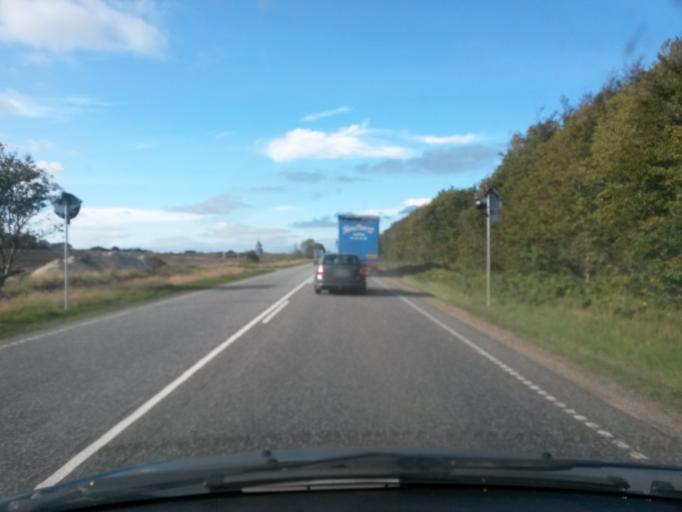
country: DK
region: Central Jutland
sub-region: Herning Kommune
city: Avlum
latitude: 56.2957
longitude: 8.7244
